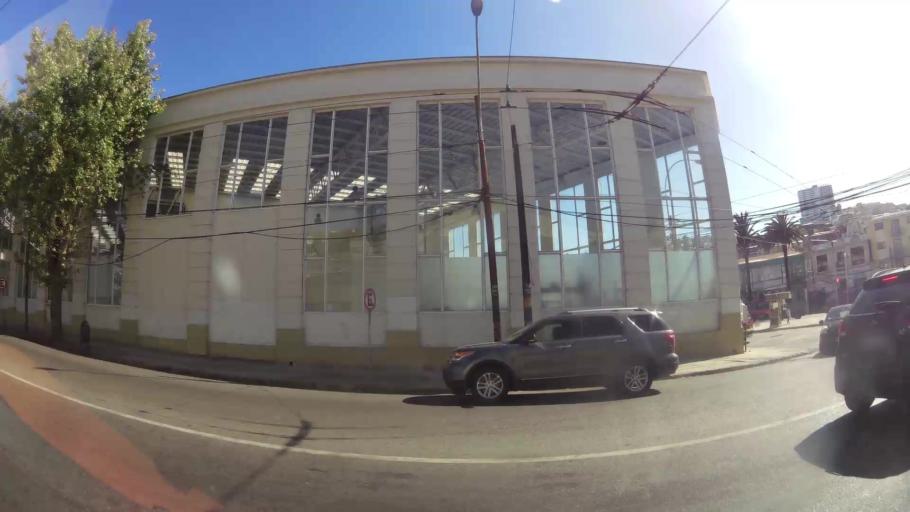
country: CL
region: Valparaiso
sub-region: Provincia de Valparaiso
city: Valparaiso
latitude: -33.0519
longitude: -71.6026
